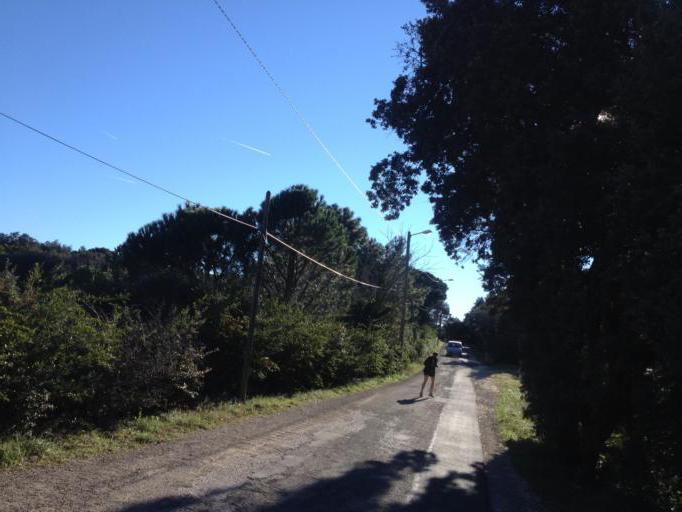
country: FR
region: Provence-Alpes-Cote d'Azur
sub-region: Departement du Vaucluse
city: Orange
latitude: 44.1225
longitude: 4.8093
